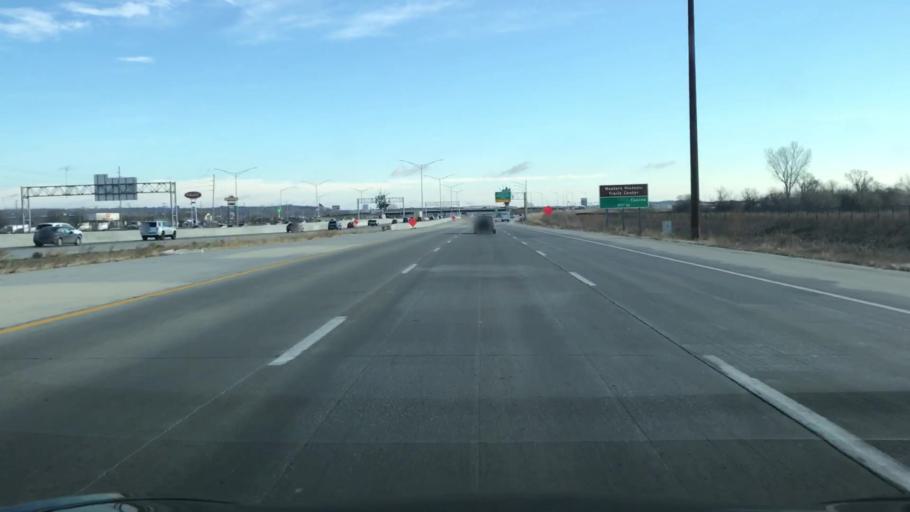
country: US
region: Iowa
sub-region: Pottawattamie County
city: Council Bluffs
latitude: 41.2322
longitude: -95.8885
